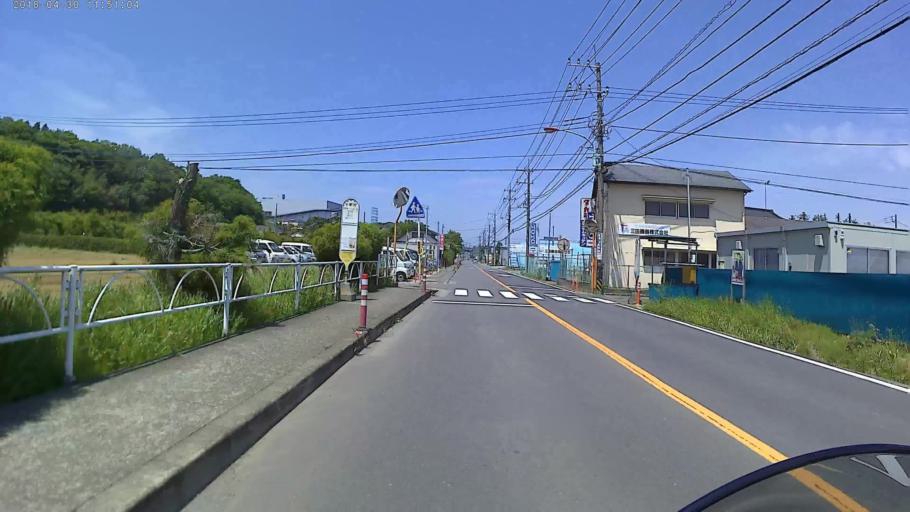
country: JP
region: Kanagawa
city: Zama
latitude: 35.4862
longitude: 139.3480
